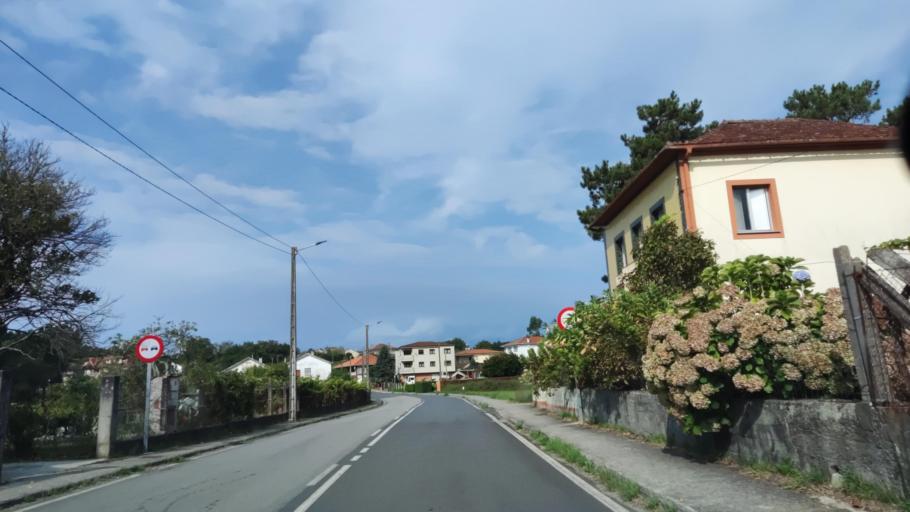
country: ES
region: Galicia
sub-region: Provincia da Coruna
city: Rianxo
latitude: 42.6478
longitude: -8.8024
